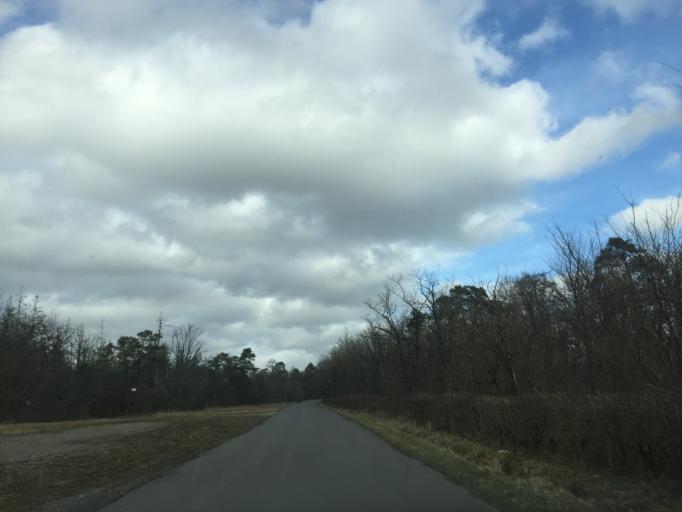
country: BE
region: Wallonia
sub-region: Province du Luxembourg
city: Durbuy
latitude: 50.3142
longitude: 5.4856
